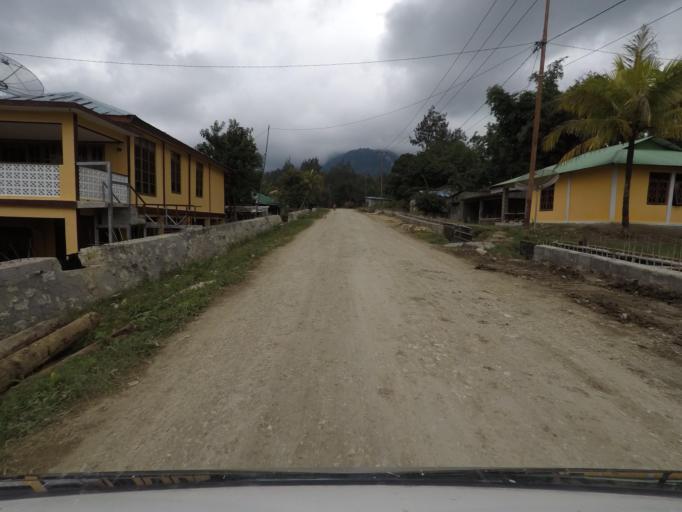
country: TL
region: Baucau
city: Venilale
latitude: -8.7393
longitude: 126.3791
